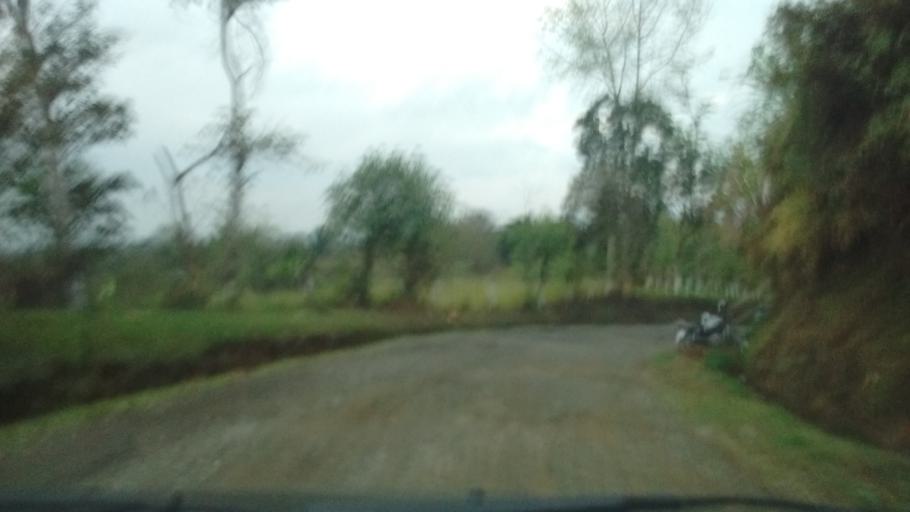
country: CO
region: Cauca
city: Lopez
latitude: 2.3859
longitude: -76.7291
